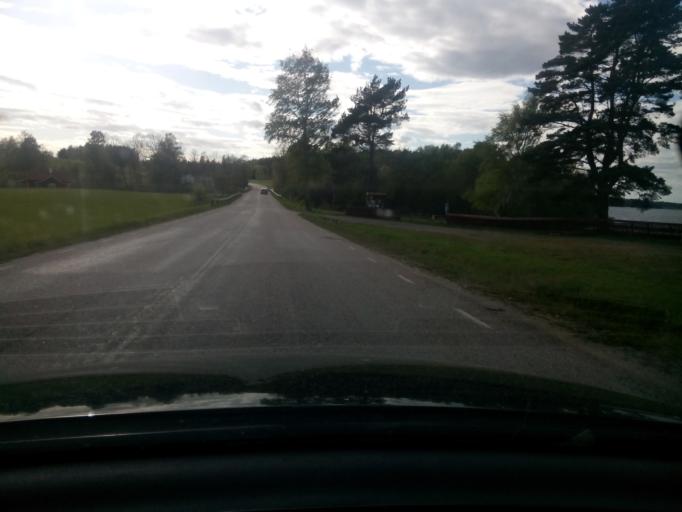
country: SE
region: Soedermanland
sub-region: Nykopings Kommun
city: Stigtomta
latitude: 58.9505
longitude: 16.8853
